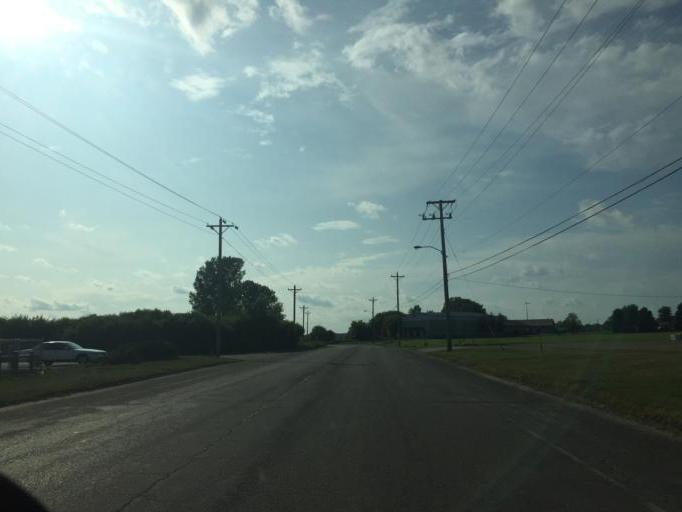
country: US
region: Minnesota
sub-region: Olmsted County
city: Rochester
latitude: 44.0357
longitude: -92.4982
